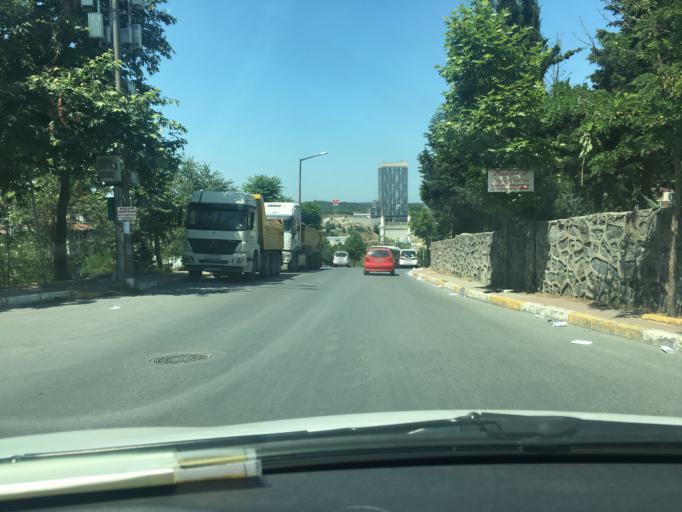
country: TR
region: Istanbul
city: Sisli
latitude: 41.0826
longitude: 28.9443
